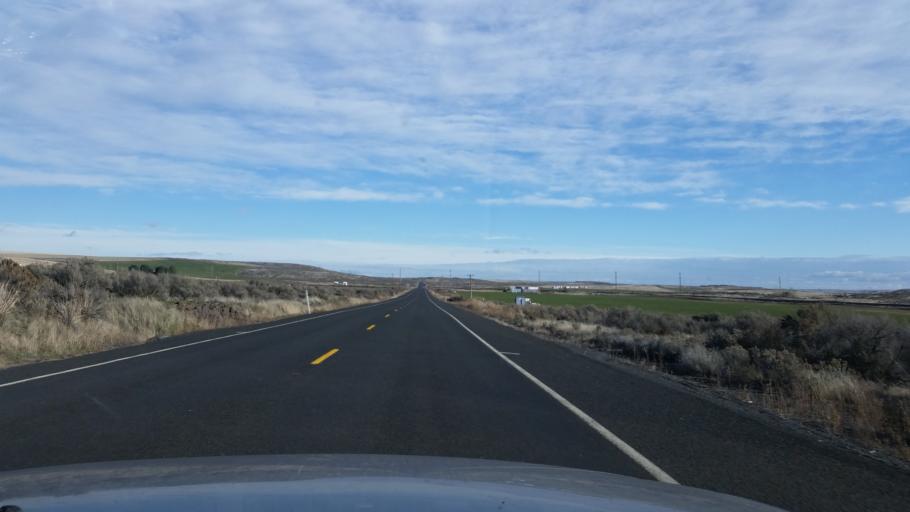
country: US
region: Washington
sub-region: Adams County
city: Ritzville
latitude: 47.3373
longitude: -118.6443
